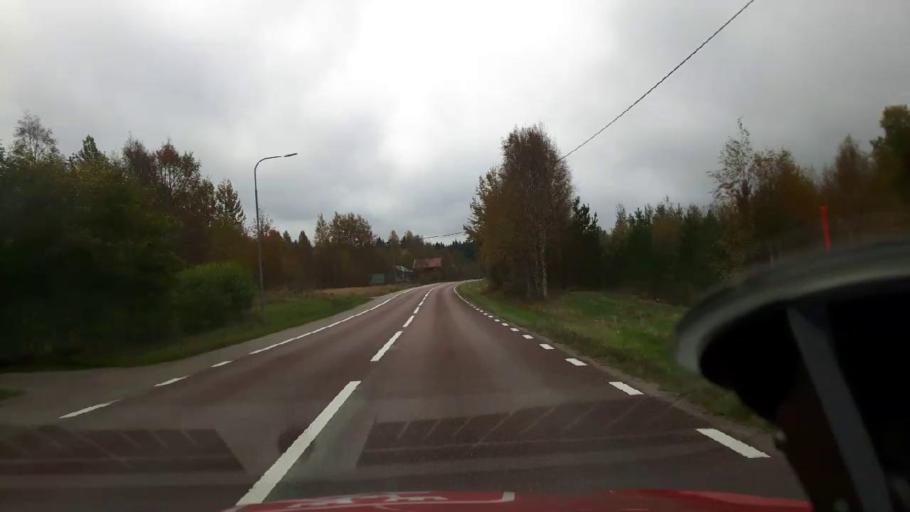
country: SE
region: Jaemtland
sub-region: Harjedalens Kommun
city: Sveg
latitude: 62.2945
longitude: 14.7870
